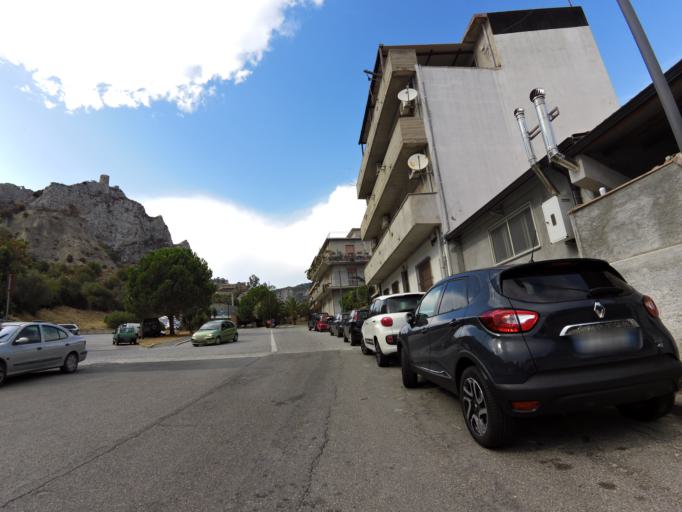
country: IT
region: Calabria
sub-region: Provincia di Reggio Calabria
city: Roccella Ionica
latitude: 38.3255
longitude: 16.4098
